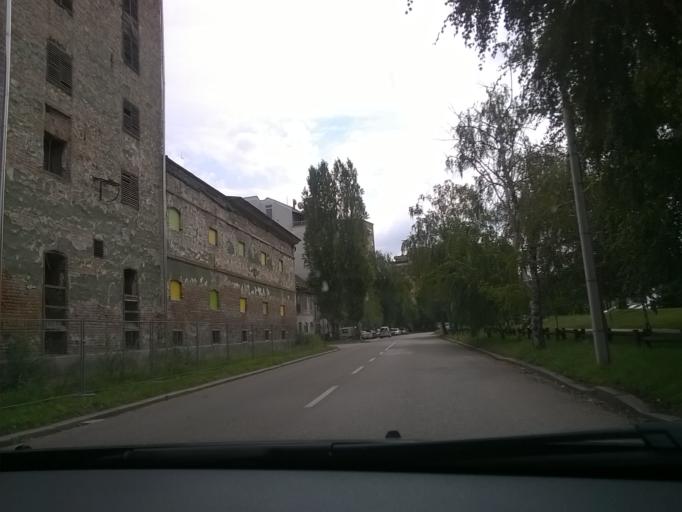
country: RS
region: Autonomna Pokrajina Vojvodina
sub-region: Juznobanatski Okrug
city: Pancevo
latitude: 44.8685
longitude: 20.6387
